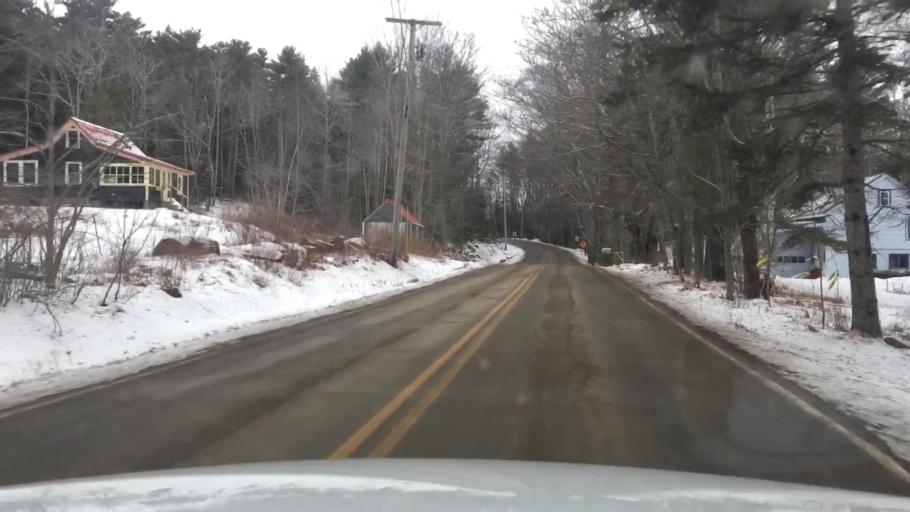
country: US
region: Maine
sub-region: Waldo County
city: Lincolnville
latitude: 44.2854
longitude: -69.0158
